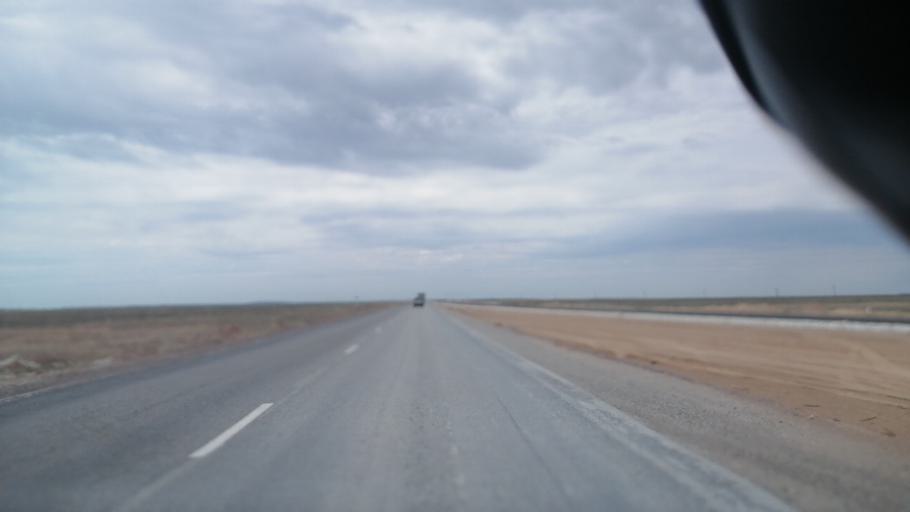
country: KZ
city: Priozersk
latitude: 46.5364
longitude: 74.1535
